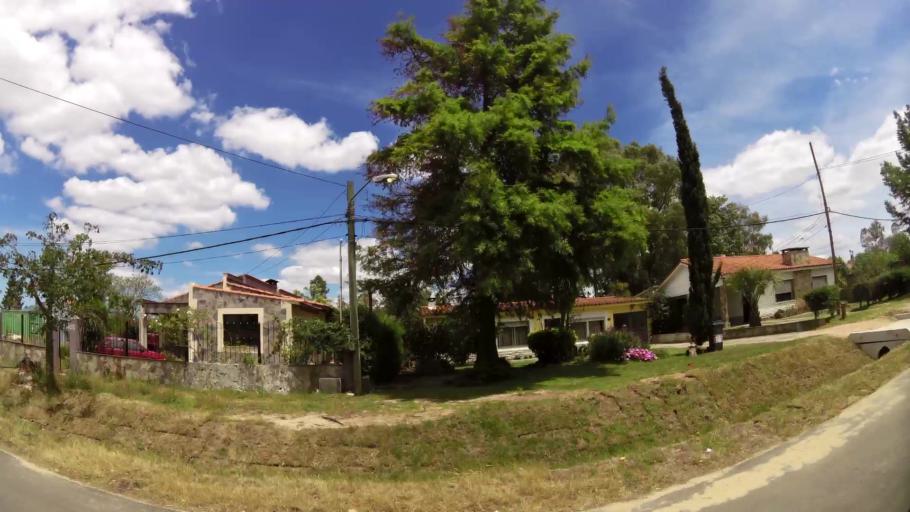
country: UY
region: Canelones
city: Colonia Nicolich
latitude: -34.8245
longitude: -55.9687
